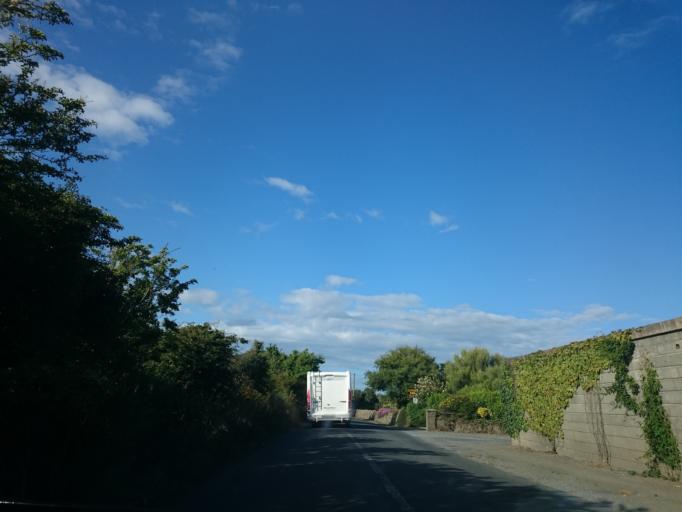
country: IE
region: Leinster
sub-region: Loch Garman
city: Loch Garman
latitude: 52.1865
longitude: -6.5690
